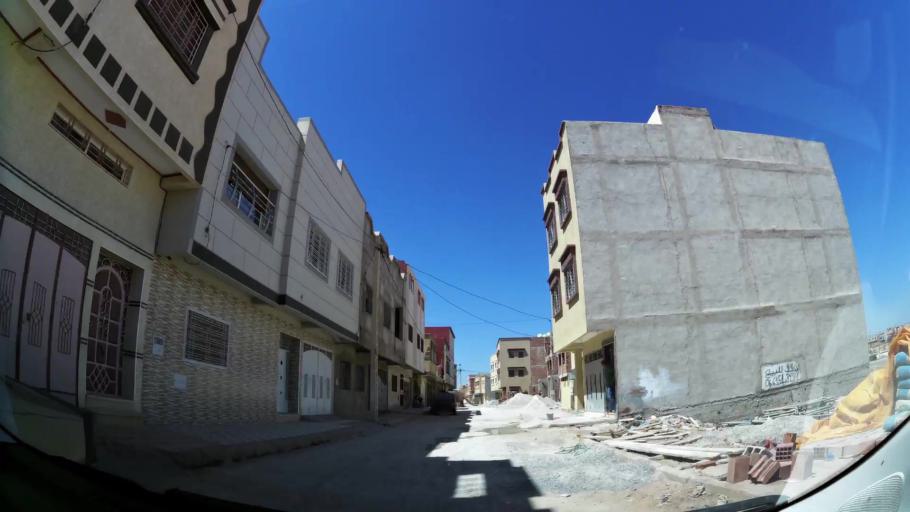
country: MA
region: Oriental
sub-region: Oujda-Angad
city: Oujda
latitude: 34.6711
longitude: -1.8661
